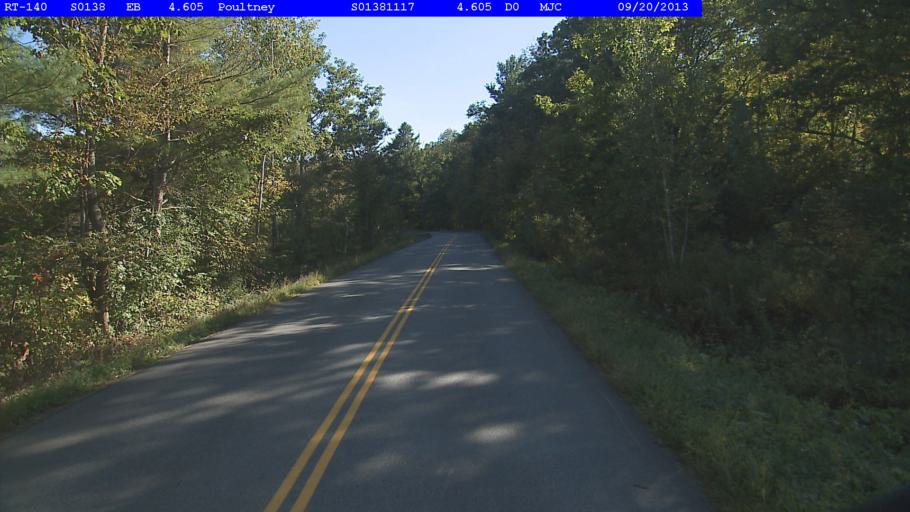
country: US
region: Vermont
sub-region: Rutland County
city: Poultney
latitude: 43.5000
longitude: -73.1752
